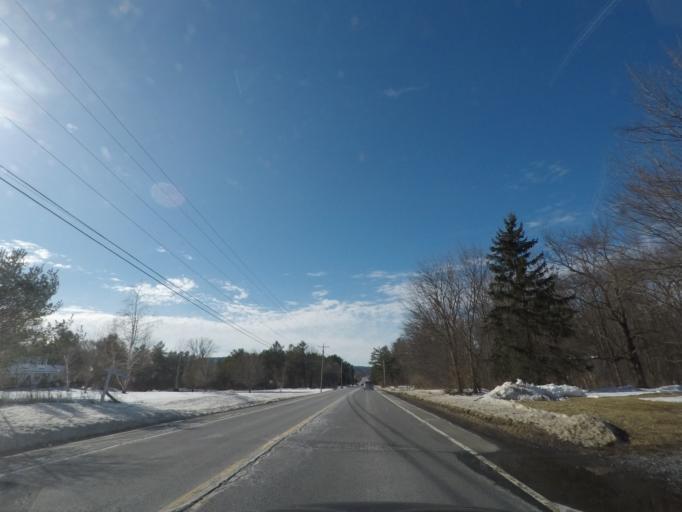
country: US
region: New York
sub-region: Albany County
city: Altamont
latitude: 42.7374
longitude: -73.9988
